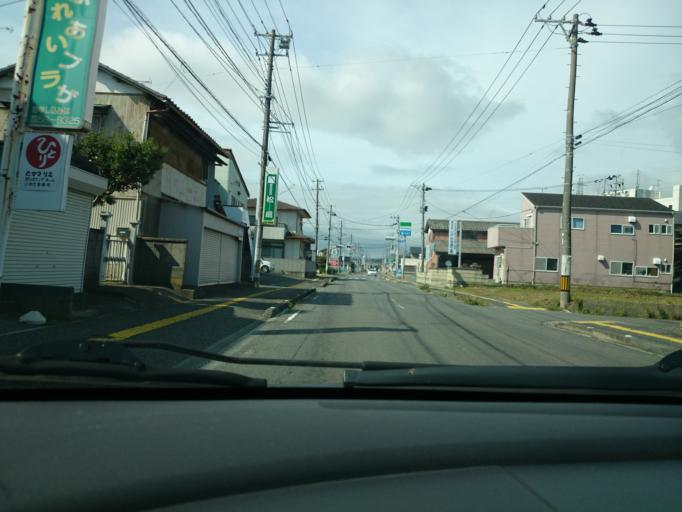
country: JP
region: Fukushima
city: Iwaki
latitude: 36.9603
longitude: 140.8976
